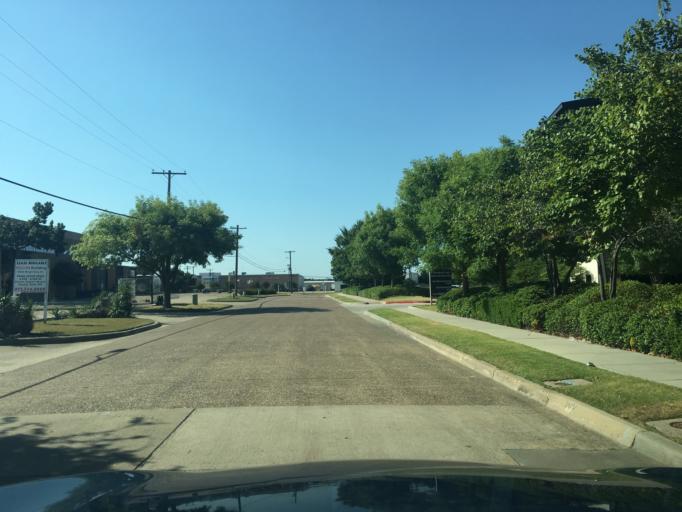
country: US
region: Texas
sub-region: Dallas County
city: Addison
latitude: 32.9619
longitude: -96.8366
